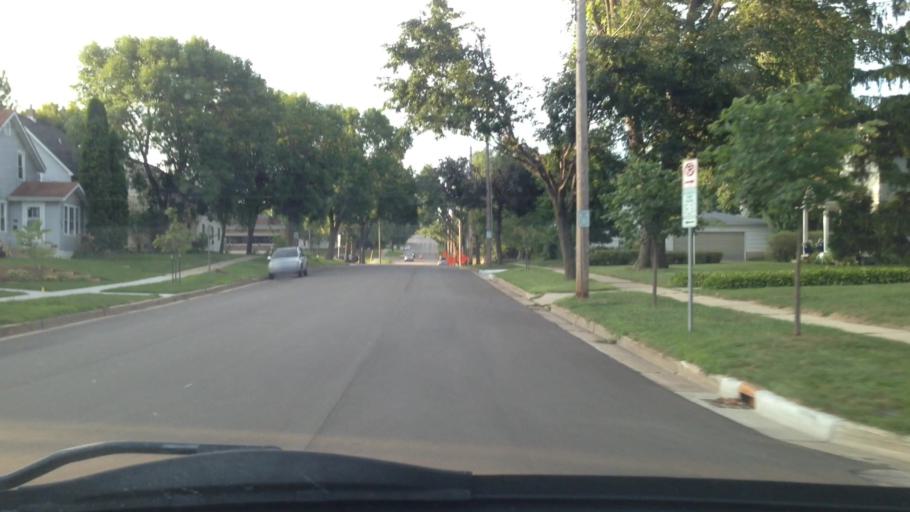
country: US
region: Minnesota
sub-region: Olmsted County
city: Rochester
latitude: 44.0148
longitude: -92.4713
